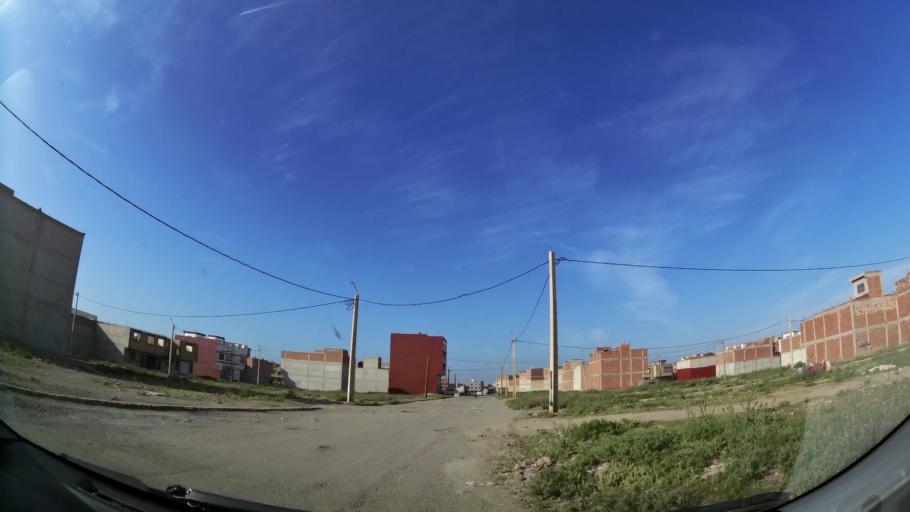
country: MA
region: Oriental
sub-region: Oujda-Angad
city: Oujda
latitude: 34.7155
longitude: -1.9002
